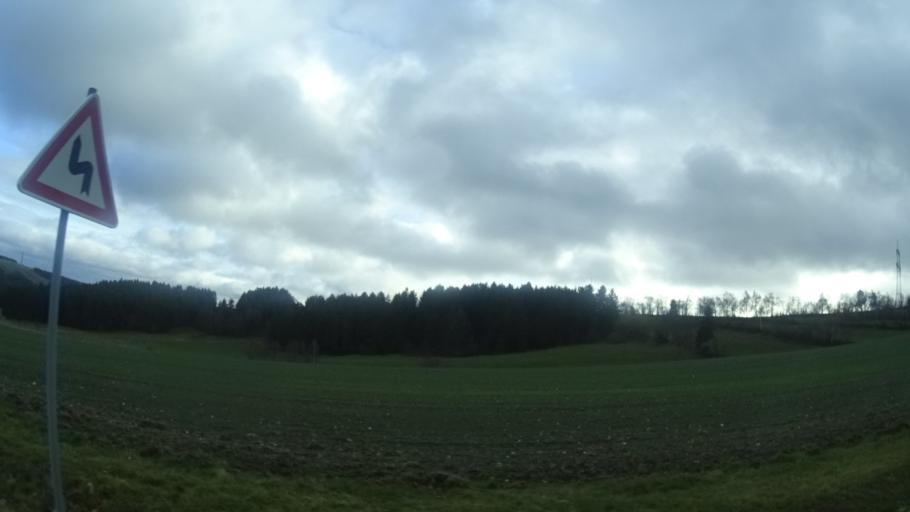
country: DE
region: Thuringia
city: Wittgendorf
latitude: 50.6045
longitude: 11.2724
